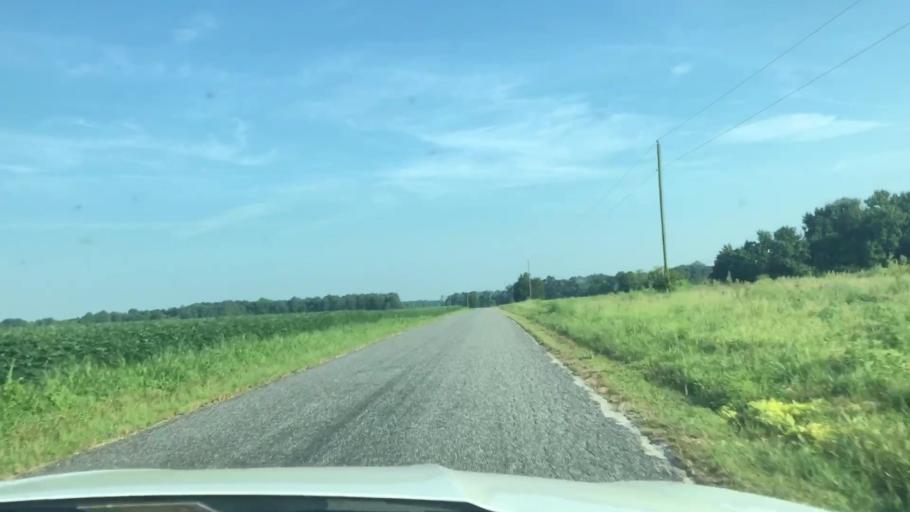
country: US
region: Virginia
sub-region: Middlesex County
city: Saluda
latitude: 37.6434
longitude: -76.6762
